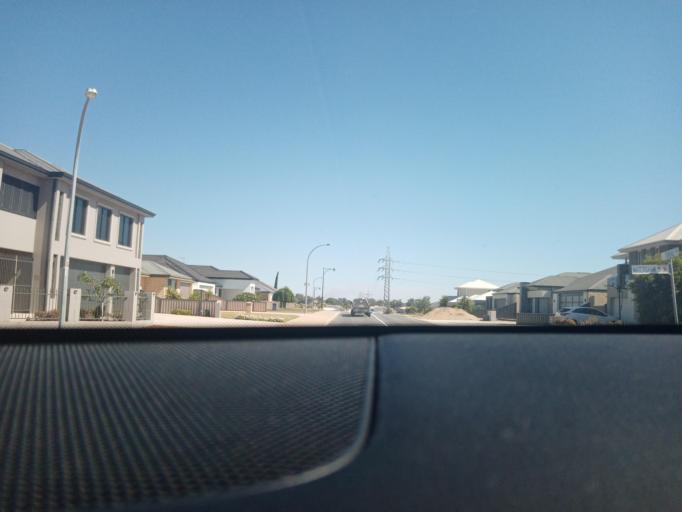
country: AU
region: Western Australia
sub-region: City of Cockburn
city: Beeliar
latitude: -32.1300
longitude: 115.8083
